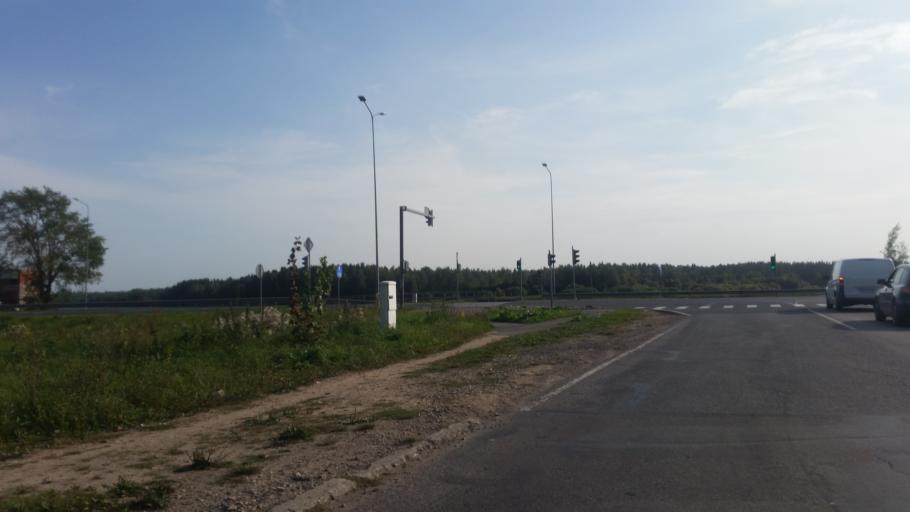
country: LV
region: Ogre
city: Ogre
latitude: 56.8194
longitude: 24.5639
